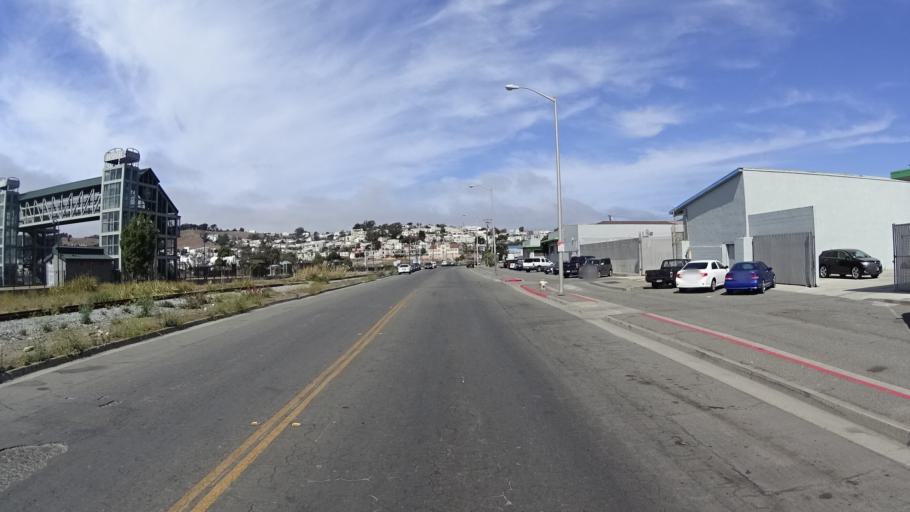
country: US
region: California
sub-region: San Mateo County
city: Brisbane
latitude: 37.7071
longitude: -122.4012
